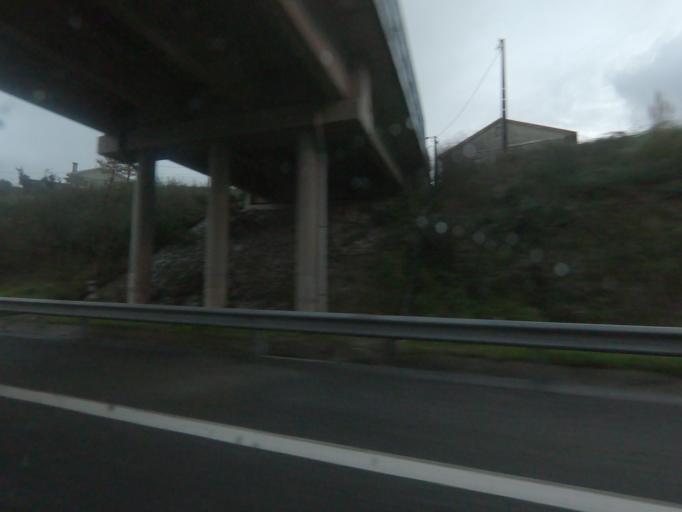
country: PT
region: Braga
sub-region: Braga
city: Oliveira
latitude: 41.5351
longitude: -8.4938
